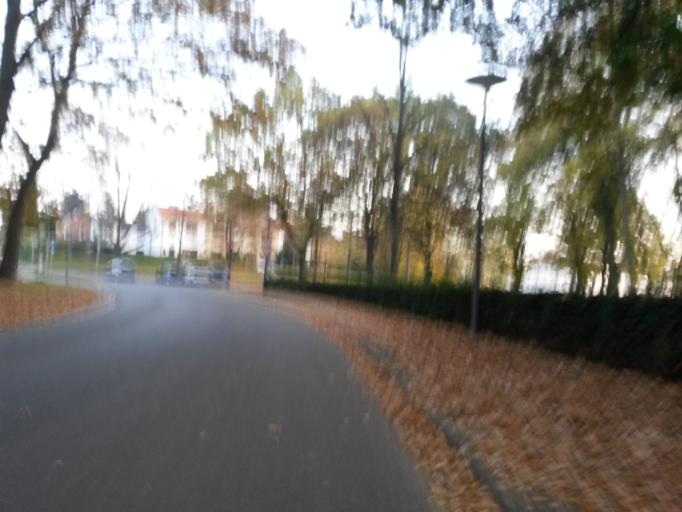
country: DE
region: Bremen
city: Bremen
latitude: 53.0528
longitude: 8.8207
